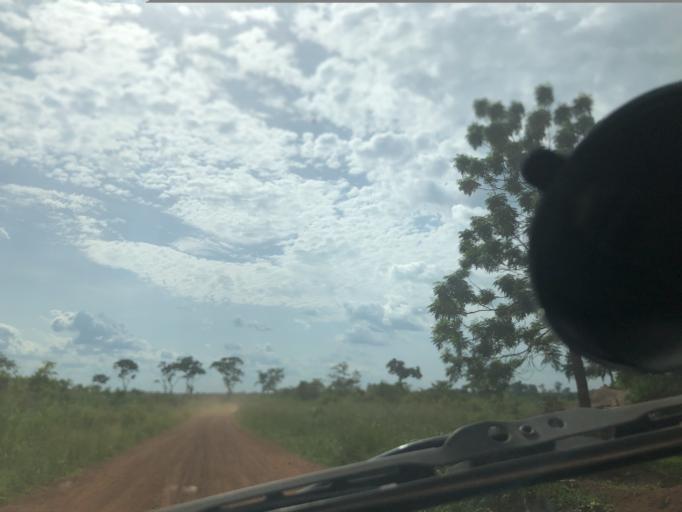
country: CF
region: Bangui
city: Bangui
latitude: 4.2398
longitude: 18.6442
